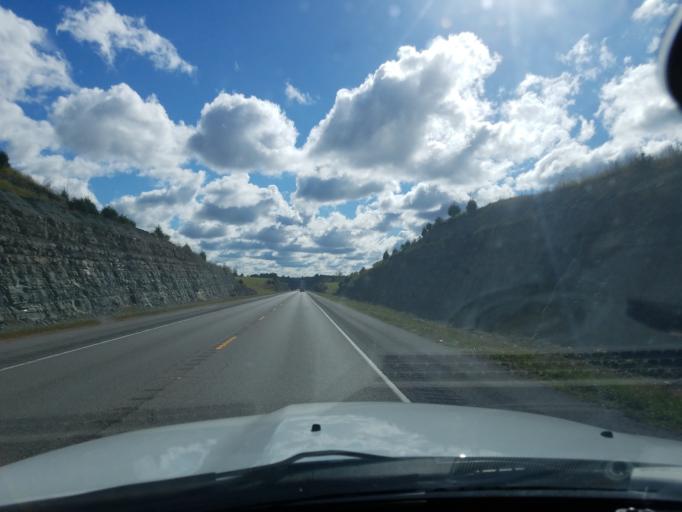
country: US
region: Kentucky
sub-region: Lincoln County
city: Stanford
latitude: 37.5104
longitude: -84.5923
